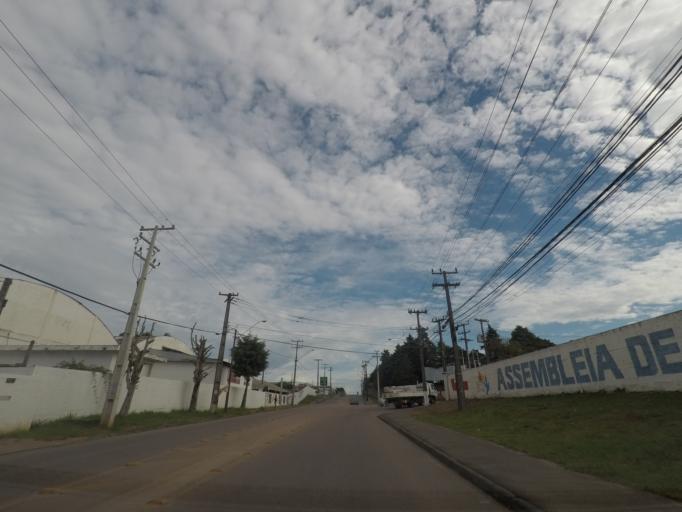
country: BR
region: Parana
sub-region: Araucaria
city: Araucaria
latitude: -25.6412
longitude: -49.3034
